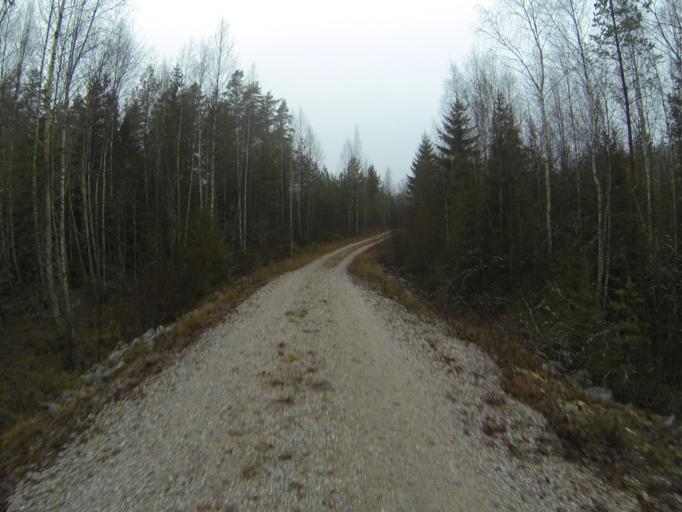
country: FI
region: Varsinais-Suomi
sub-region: Salo
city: Halikko
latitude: 60.4069
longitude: 22.9826
